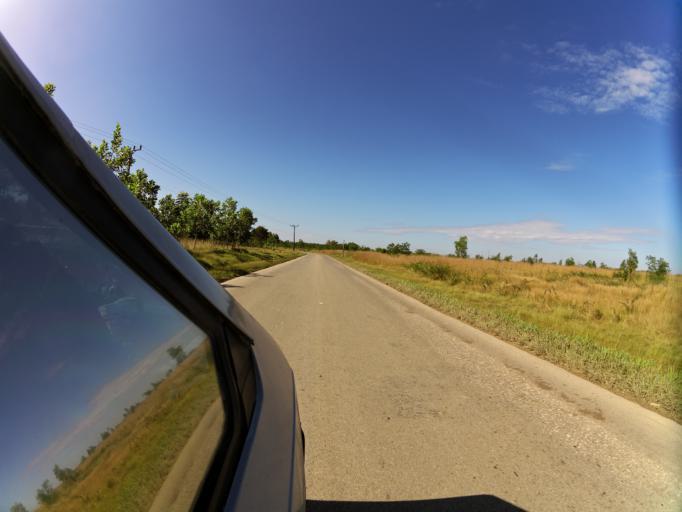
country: CU
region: Las Tunas
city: Las Tunas
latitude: 20.9801
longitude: -76.9012
